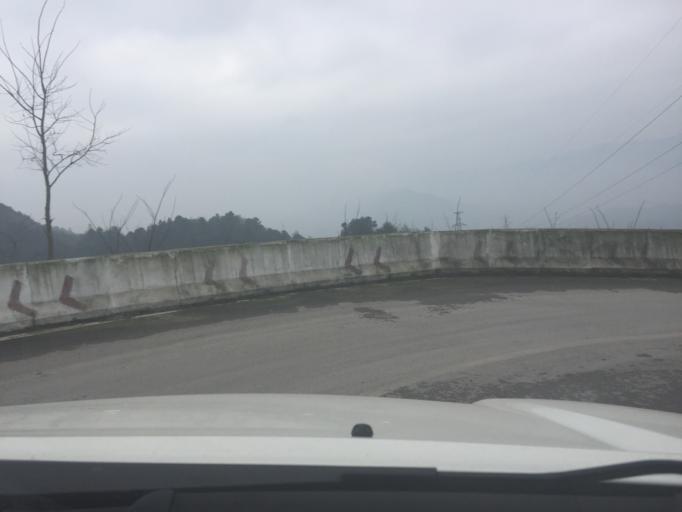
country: CN
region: Guizhou Sheng
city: Supu
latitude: 27.1004
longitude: 106.8123
